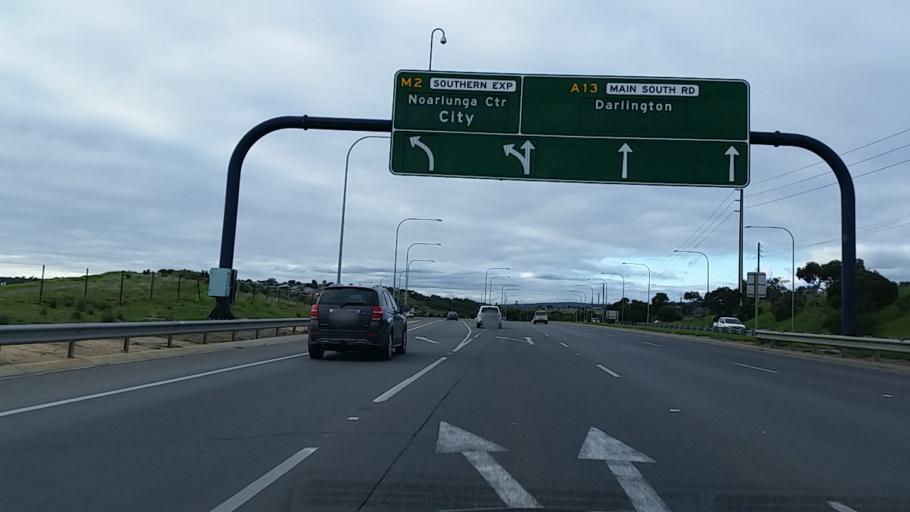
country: AU
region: South Australia
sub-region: Onkaparinga
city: Noarlunga
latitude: -35.1676
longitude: 138.5063
